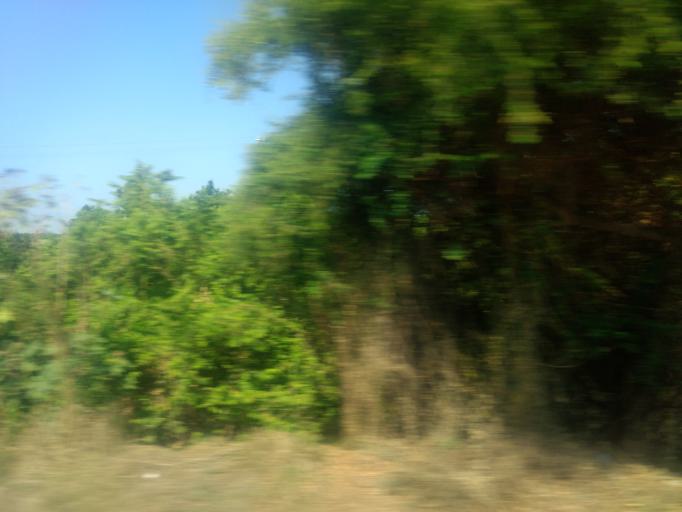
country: MX
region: Colima
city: El Colomo
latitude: 19.0417
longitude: -104.2594
